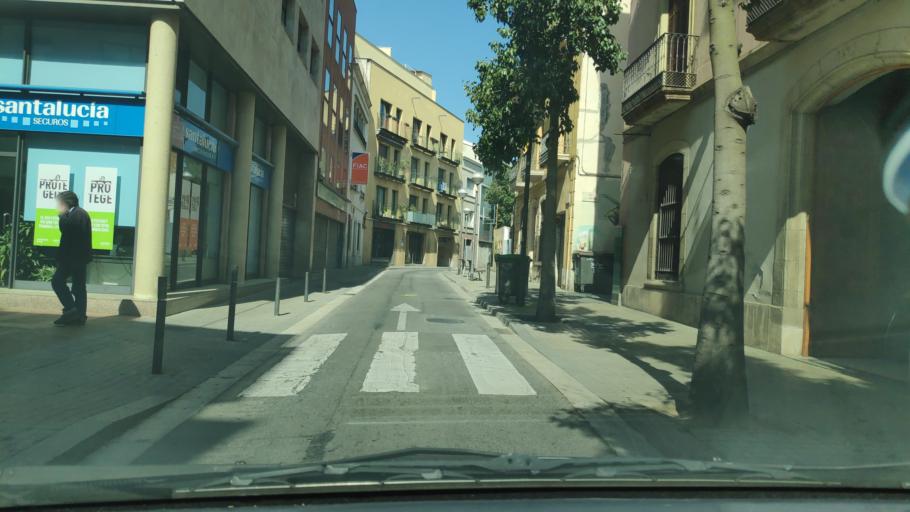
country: ES
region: Catalonia
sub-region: Provincia de Barcelona
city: Sabadell
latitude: 41.5488
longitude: 2.1093
